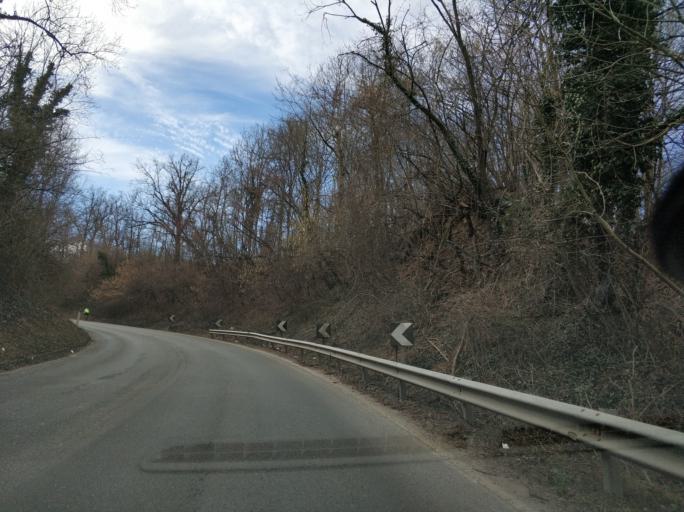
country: IT
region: Piedmont
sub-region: Provincia di Torino
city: Lombardore
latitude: 45.2308
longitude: 7.7325
